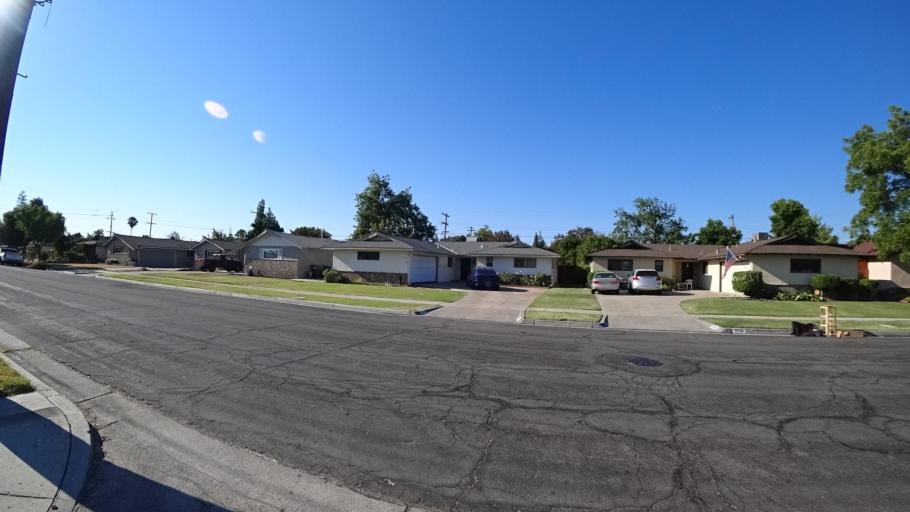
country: US
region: California
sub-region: Fresno County
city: Fresno
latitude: 36.7891
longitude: -119.7649
